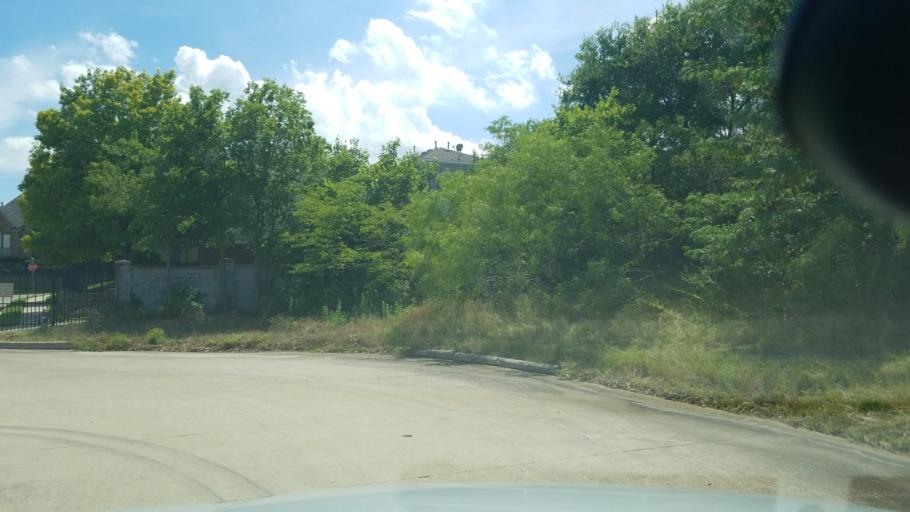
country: US
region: Texas
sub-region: Dallas County
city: Irving
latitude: 32.8515
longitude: -96.9305
